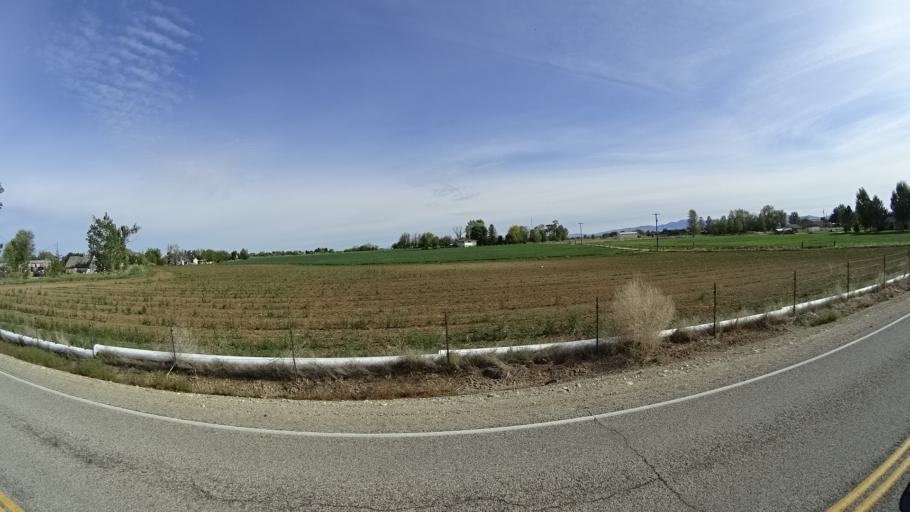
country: US
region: Idaho
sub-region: Ada County
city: Kuna
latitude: 43.4736
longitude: -116.3654
